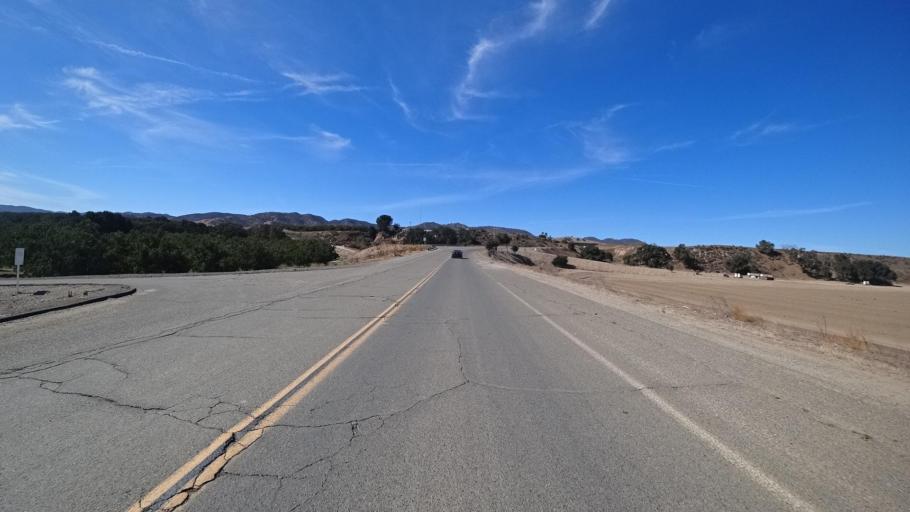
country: US
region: California
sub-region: Monterey County
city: King City
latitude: 36.0146
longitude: -120.9175
